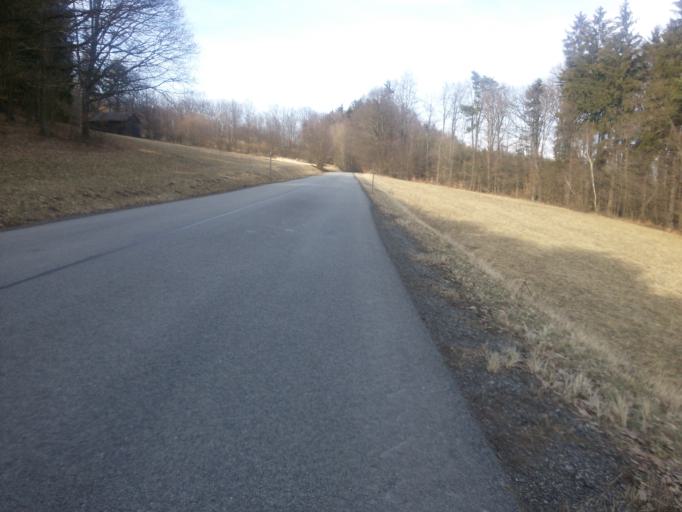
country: CZ
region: South Moravian
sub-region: Okres Brno-Venkov
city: Lomnice
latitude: 49.4241
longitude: 16.4089
